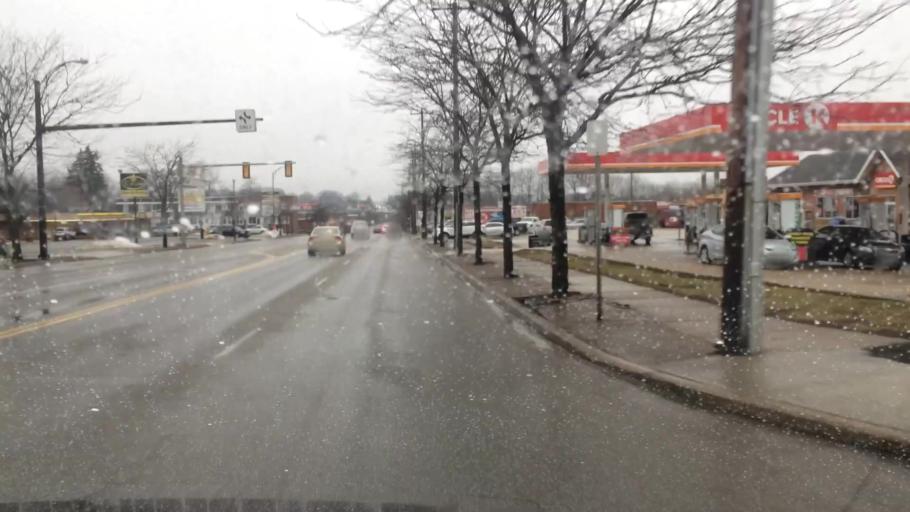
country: US
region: Ohio
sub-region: Summit County
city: Cuyahoga Falls
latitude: 41.1022
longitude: -81.4805
